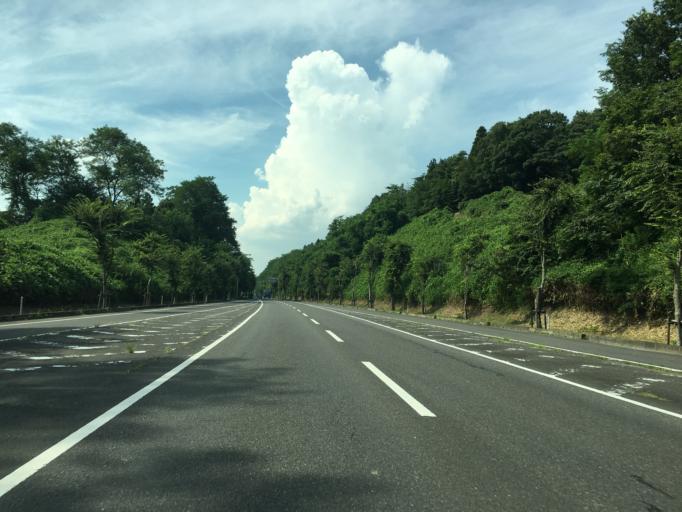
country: JP
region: Fukushima
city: Sukagawa
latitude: 37.2445
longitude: 140.4337
